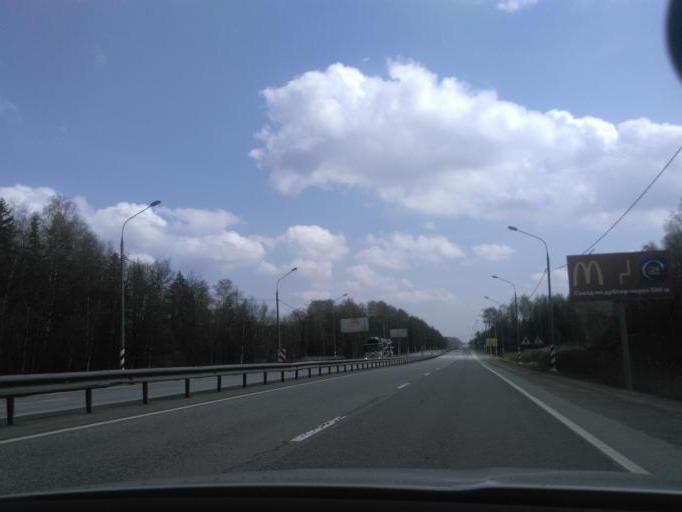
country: RU
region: Moskovskaya
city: Chashnikovo
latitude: 56.0213
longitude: 37.1908
